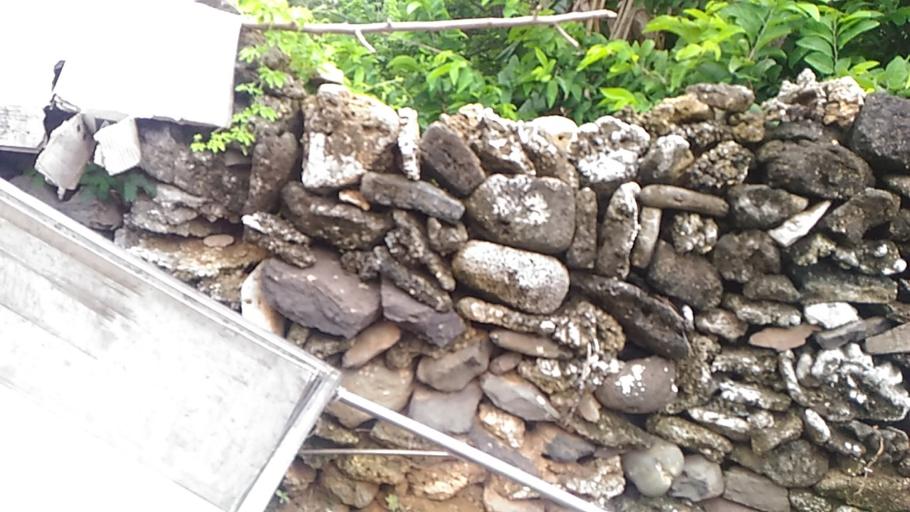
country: TW
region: Taiwan
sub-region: Penghu
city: Ma-kung
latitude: 23.3733
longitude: 119.4962
